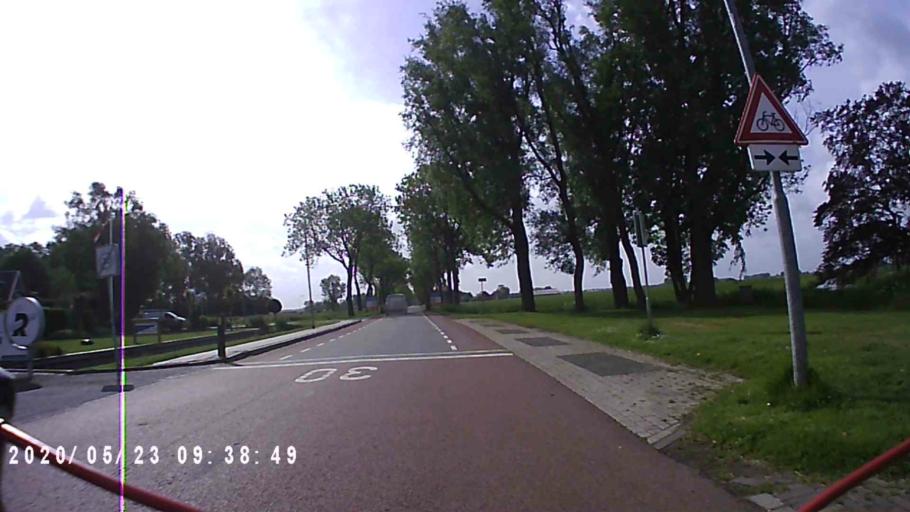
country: NL
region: Groningen
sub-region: Gemeente Slochteren
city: Slochteren
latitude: 53.2956
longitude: 6.7328
